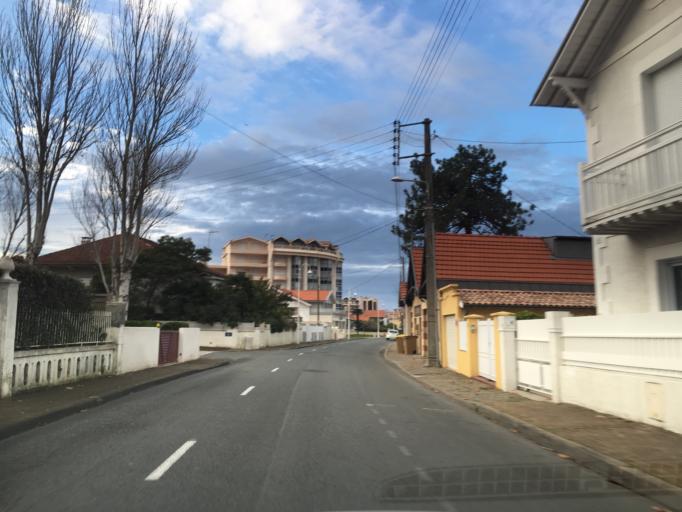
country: FR
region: Aquitaine
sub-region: Departement de la Gironde
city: Arcachon
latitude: 44.6582
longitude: -1.1506
